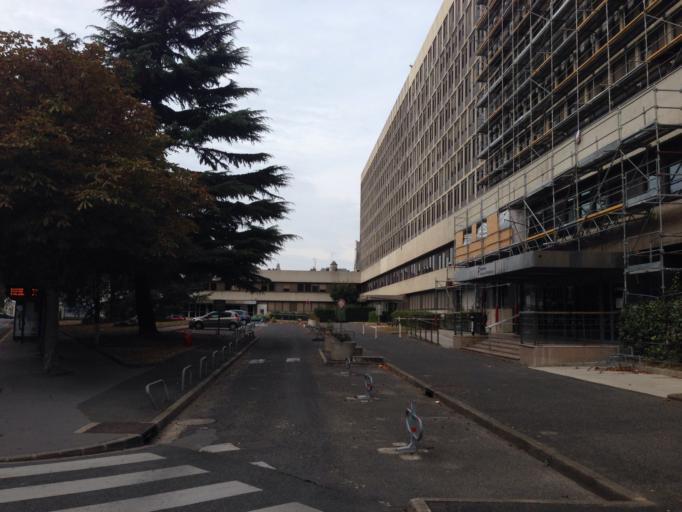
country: FR
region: Centre
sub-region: Departement d'Indre-et-Loire
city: Tours
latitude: 47.3878
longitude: 0.6974
